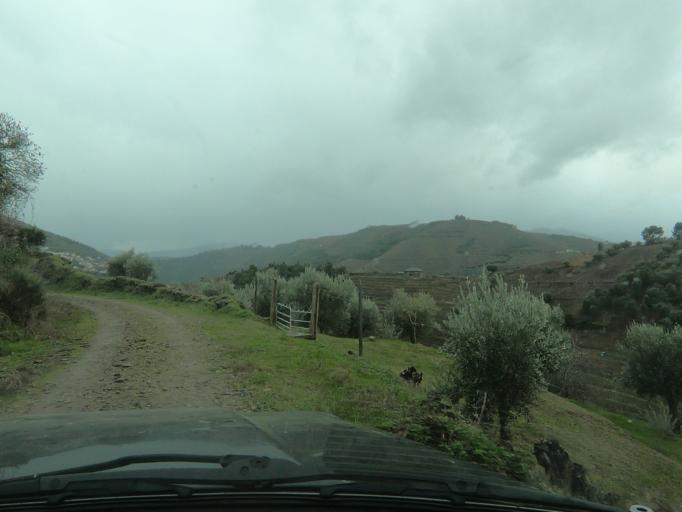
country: PT
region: Vila Real
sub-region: Santa Marta de Penaguiao
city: Santa Marta de Penaguiao
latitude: 41.2335
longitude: -7.7394
